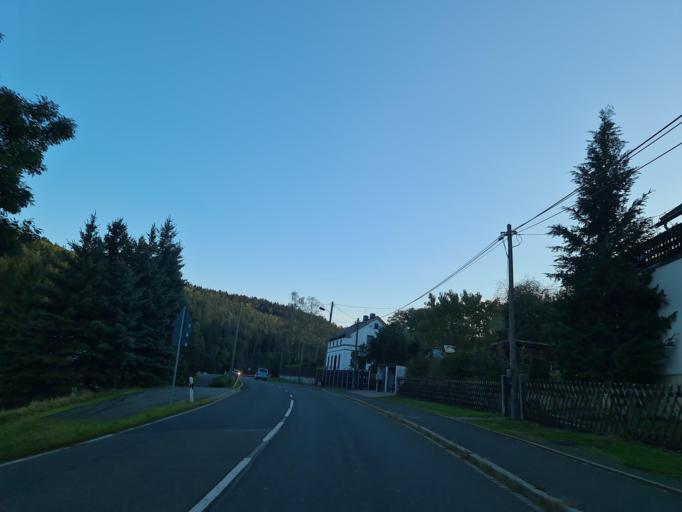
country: DE
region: Saxony
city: Elsterberg
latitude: 50.5901
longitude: 12.1377
